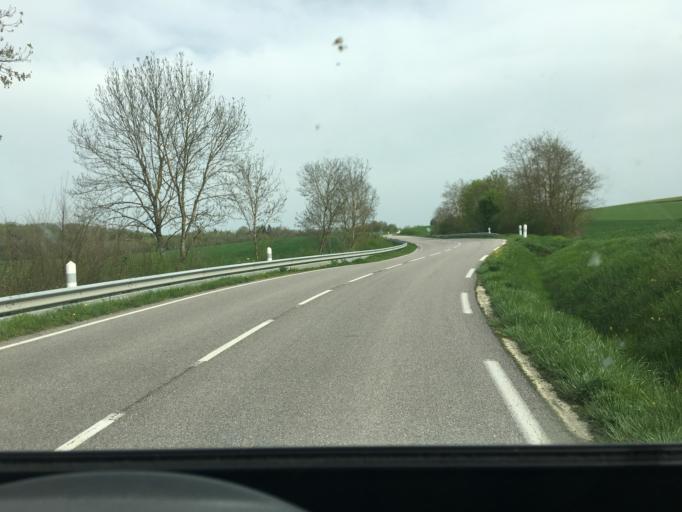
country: FR
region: Lorraine
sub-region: Departement de la Moselle
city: Vic-sur-Seille
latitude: 48.7465
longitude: 6.5395
